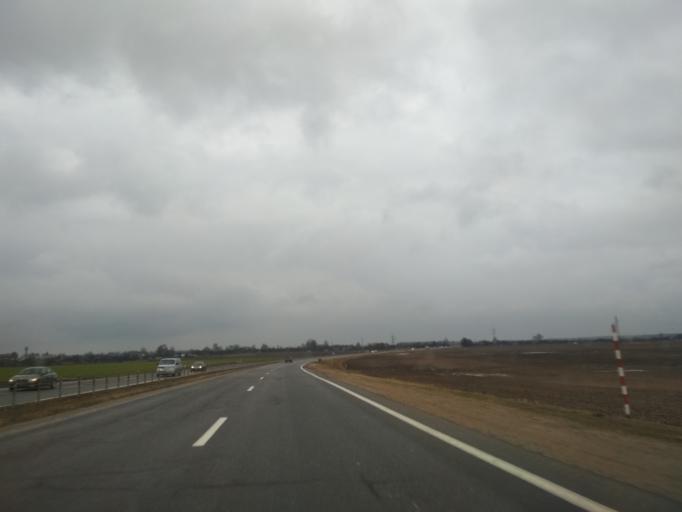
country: BY
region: Minsk
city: Dukora
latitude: 53.6779
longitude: 27.9267
